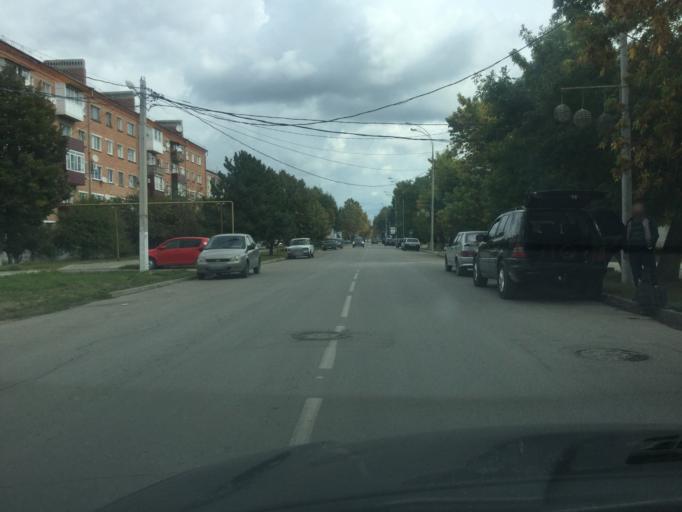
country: RU
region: Krasnodarskiy
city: Slavyansk-na-Kubani
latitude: 45.2545
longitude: 38.1136
